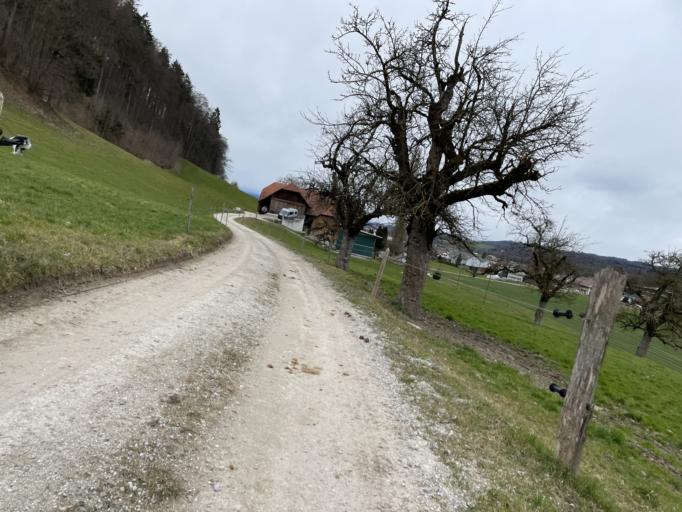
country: CH
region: Bern
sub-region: Bern-Mittelland District
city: Rubigen
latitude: 46.8838
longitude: 7.5277
